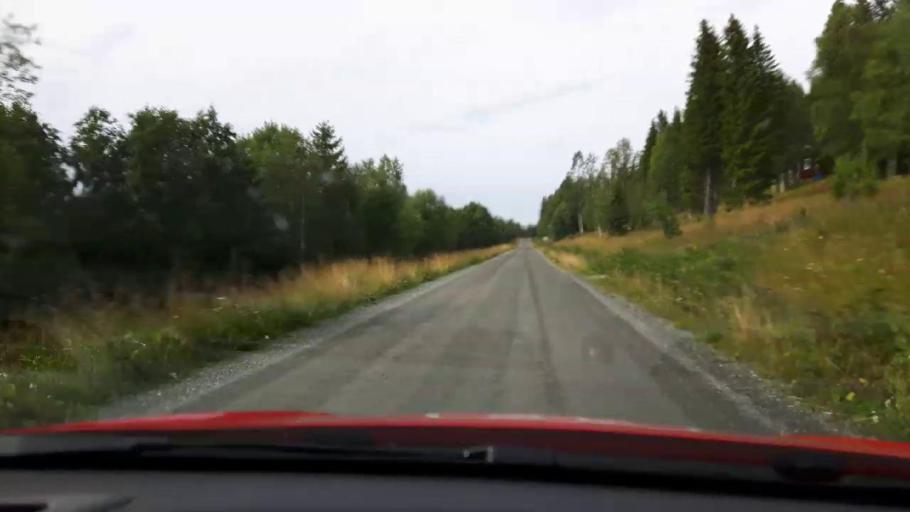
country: SE
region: Jaemtland
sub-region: Are Kommun
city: Are
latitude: 63.7456
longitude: 12.9755
